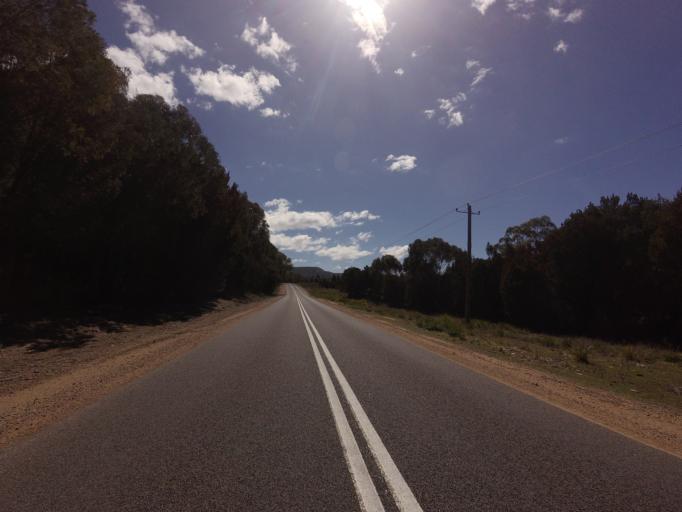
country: AU
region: Tasmania
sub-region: Break O'Day
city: St Helens
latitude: -41.6795
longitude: 148.2790
